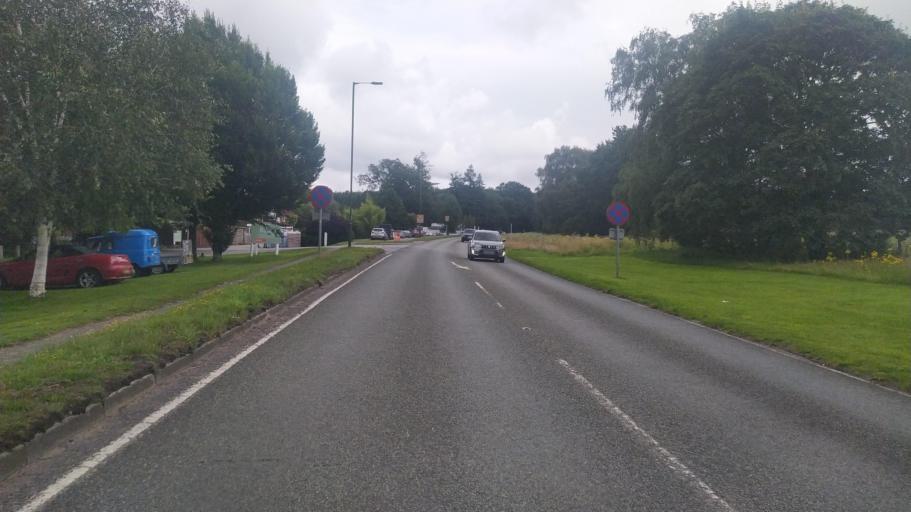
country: GB
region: England
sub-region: Hampshire
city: Liss
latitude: 51.0448
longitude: -0.8518
